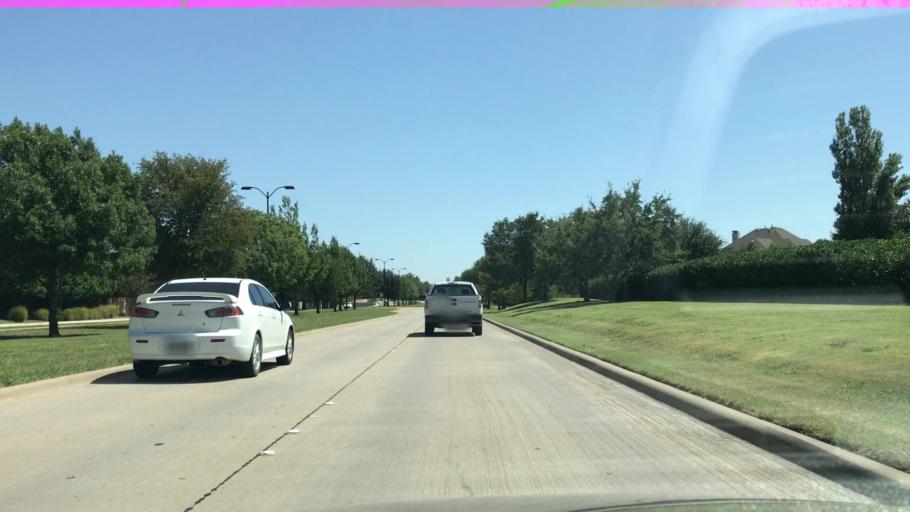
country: US
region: Texas
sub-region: Collin County
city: Frisco
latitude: 33.1532
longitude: -96.8772
